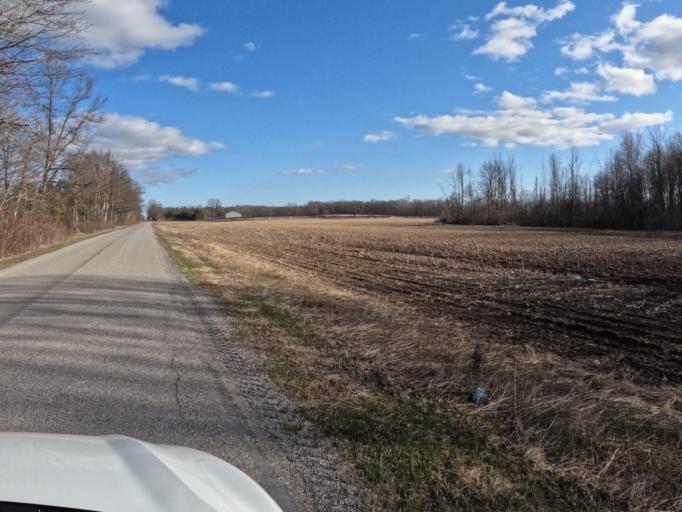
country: CA
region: Ontario
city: Norfolk County
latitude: 42.8191
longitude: -80.5682
